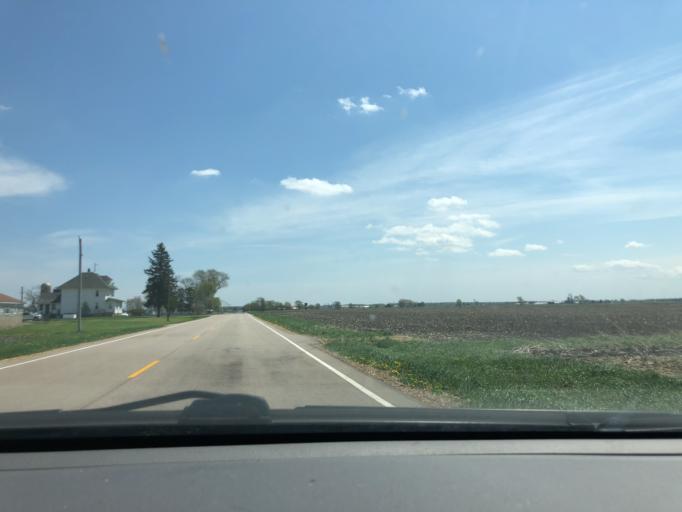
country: US
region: Illinois
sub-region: Kane County
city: Hampshire
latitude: 42.1100
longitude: -88.5867
